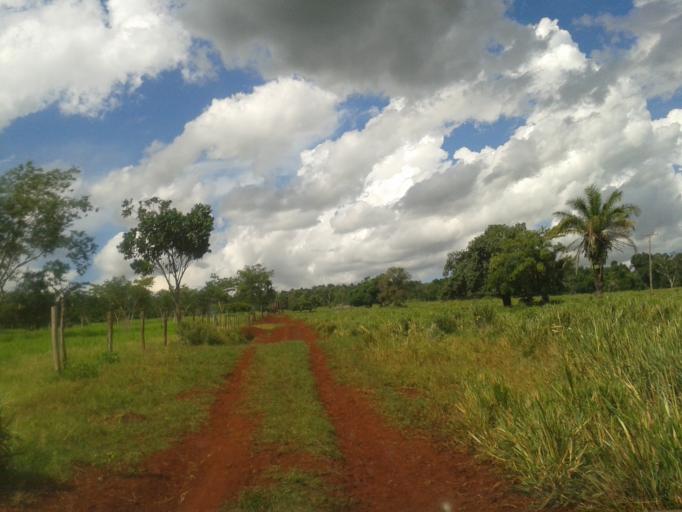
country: BR
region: Minas Gerais
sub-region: Capinopolis
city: Capinopolis
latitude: -18.7702
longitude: -49.8292
